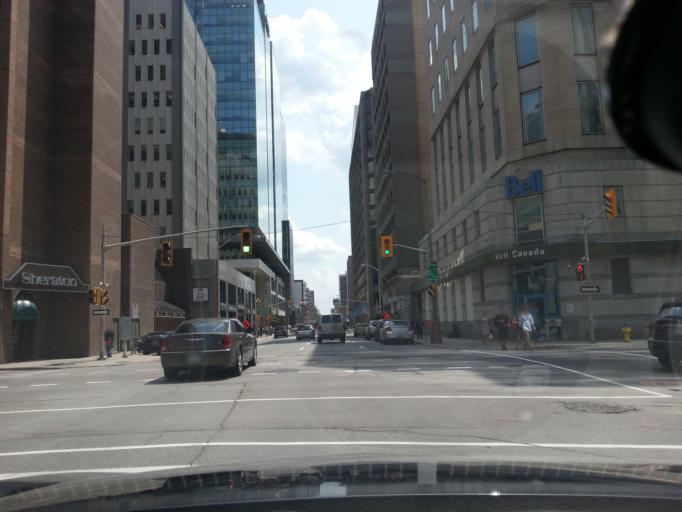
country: CA
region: Ontario
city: Ottawa
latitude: 45.4209
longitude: -75.6984
